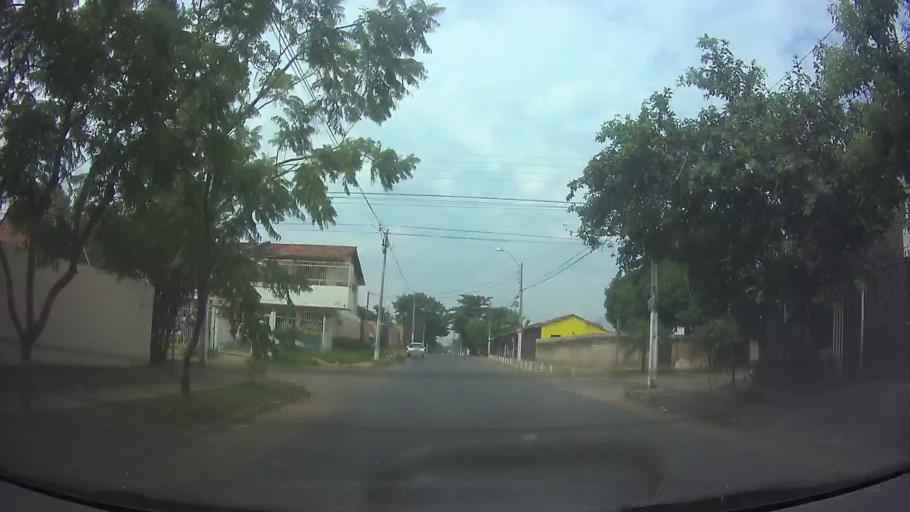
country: PY
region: Central
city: Fernando de la Mora
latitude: -25.2980
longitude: -57.5375
